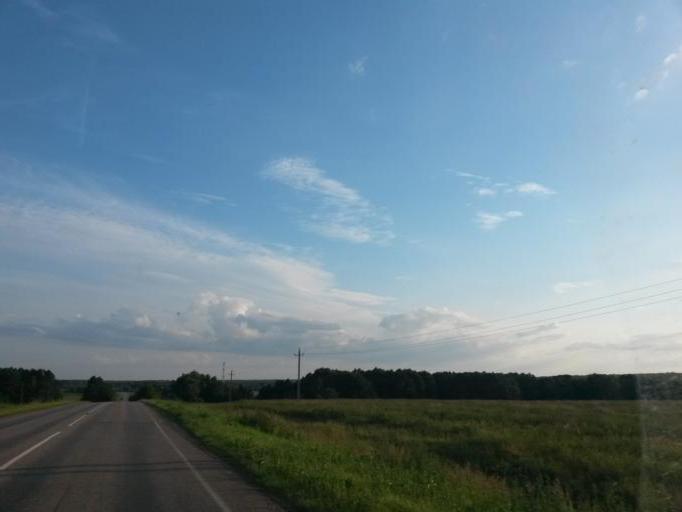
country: RU
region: Moskovskaya
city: Barybino
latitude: 55.2242
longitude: 37.7922
